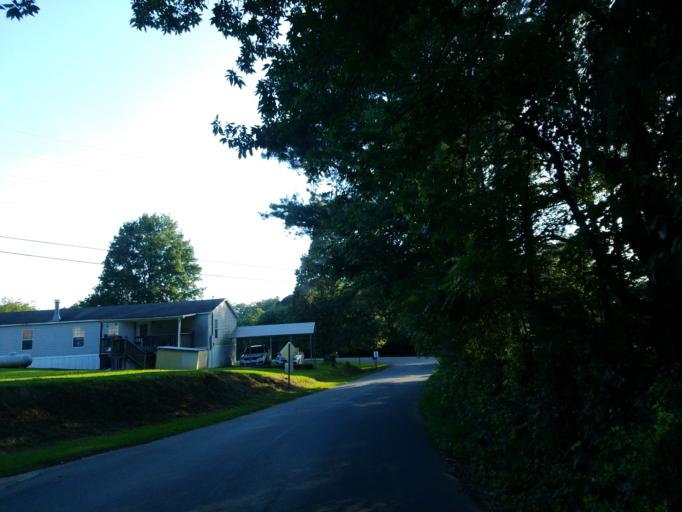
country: US
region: Georgia
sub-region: Gilmer County
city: Ellijay
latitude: 34.5944
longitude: -84.4579
